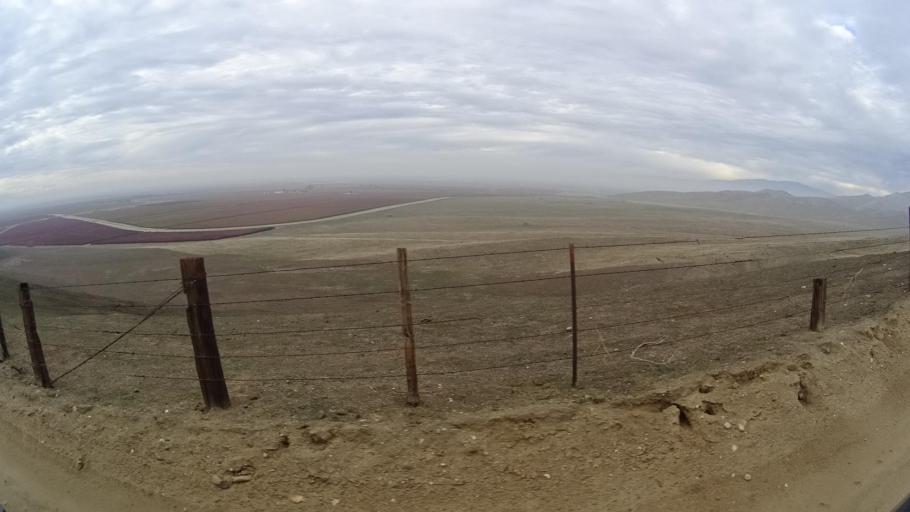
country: US
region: California
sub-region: Kern County
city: Arvin
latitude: 35.1414
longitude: -118.7989
